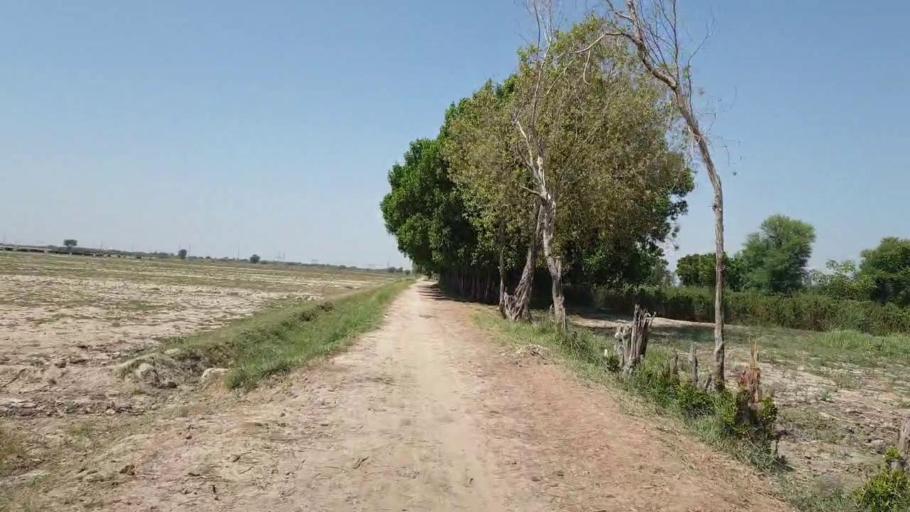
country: PK
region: Sindh
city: Hyderabad
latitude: 25.4720
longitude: 68.4241
